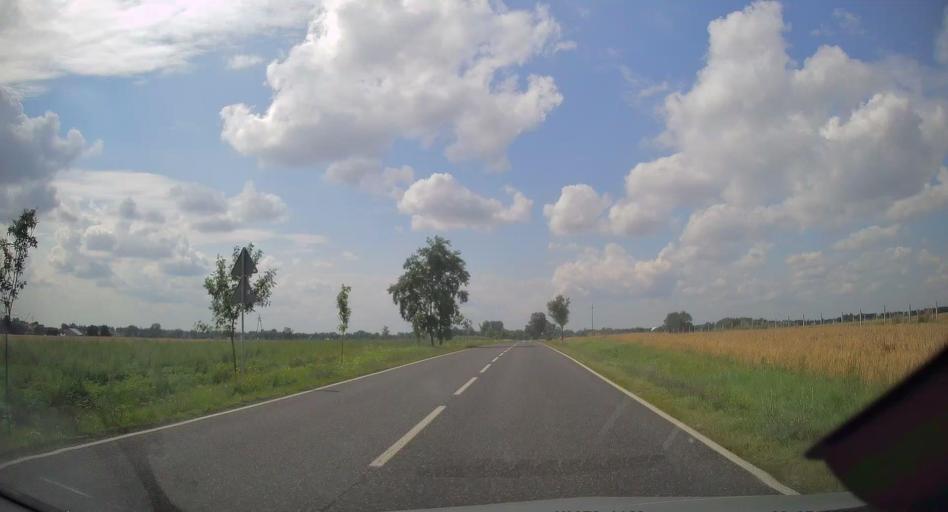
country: PL
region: Lodz Voivodeship
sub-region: Powiat skierniewicki
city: Gluchow
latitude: 51.7996
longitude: 20.0241
